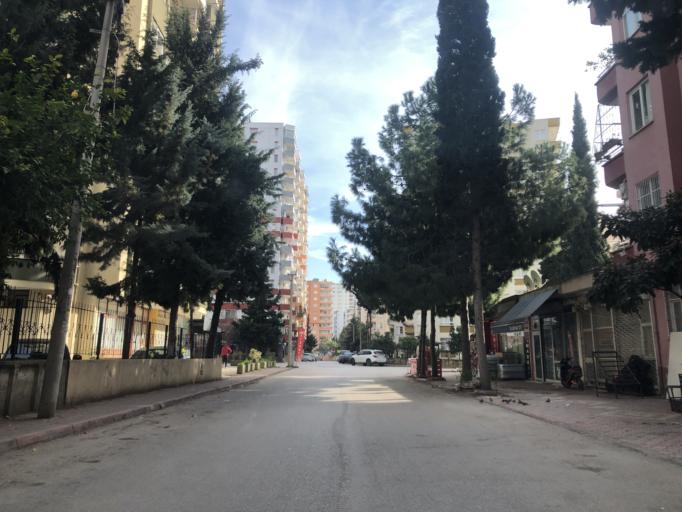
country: TR
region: Adana
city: Adana
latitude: 37.0516
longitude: 35.2907
